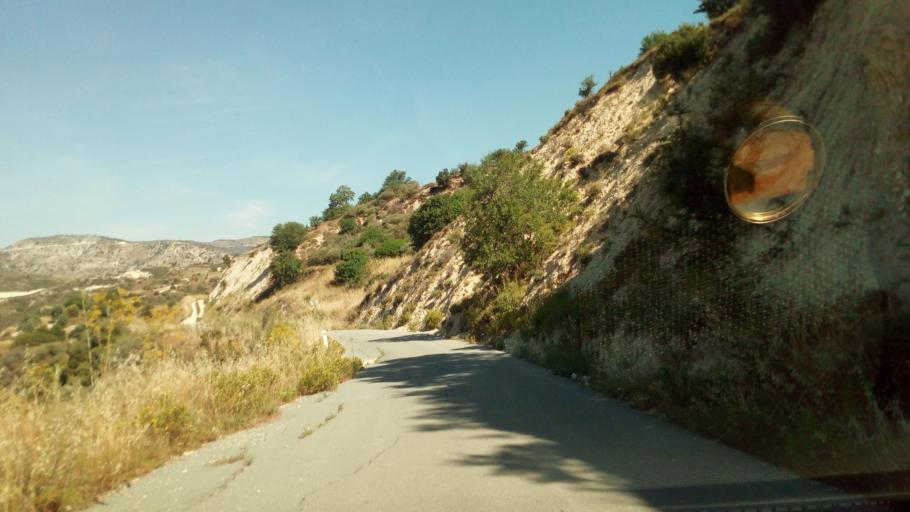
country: CY
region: Limassol
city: Pachna
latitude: 34.8140
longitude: 32.7366
